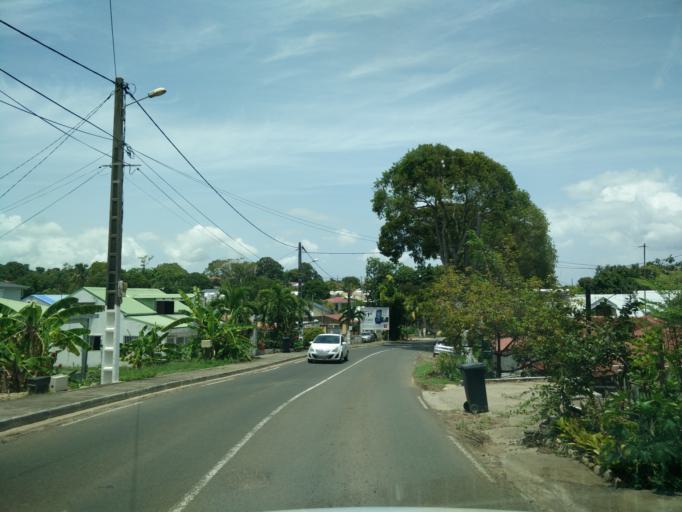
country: GP
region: Guadeloupe
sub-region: Guadeloupe
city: Petit-Bourg
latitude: 16.1856
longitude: -61.5897
